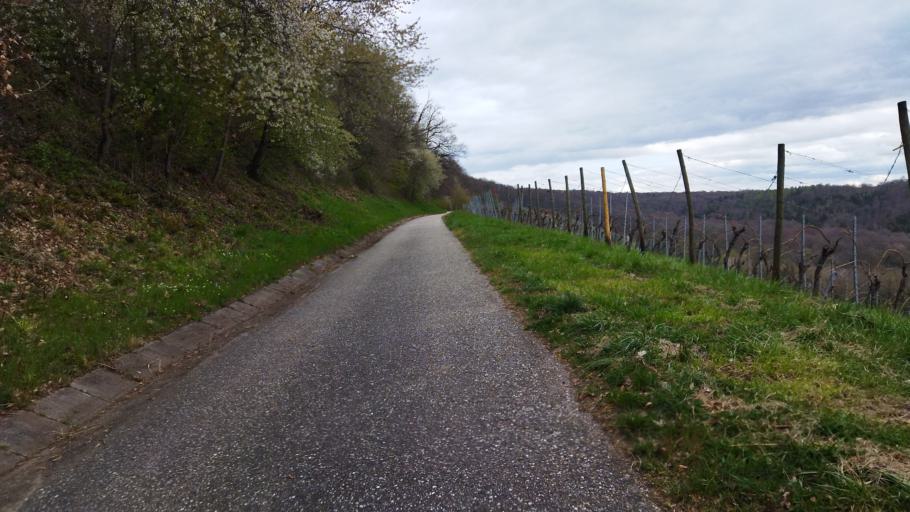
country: DE
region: Baden-Wuerttemberg
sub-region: Regierungsbezirk Stuttgart
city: Erlenbach
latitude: 49.1905
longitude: 9.2761
